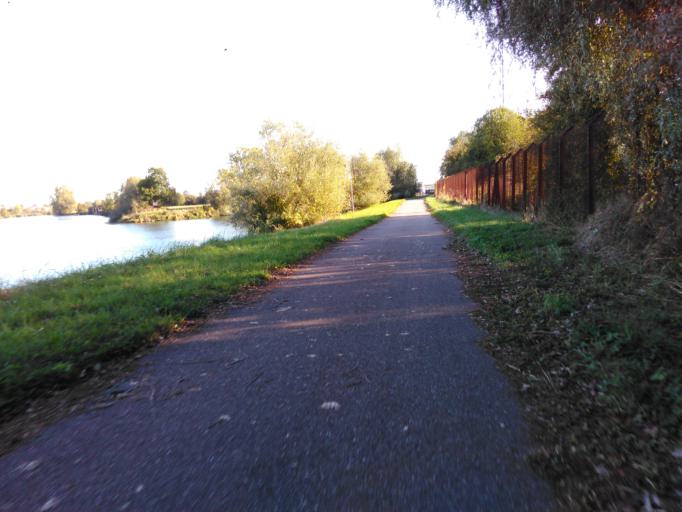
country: FR
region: Lorraine
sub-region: Departement de la Moselle
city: Bousse
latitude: 49.2869
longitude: 6.1819
